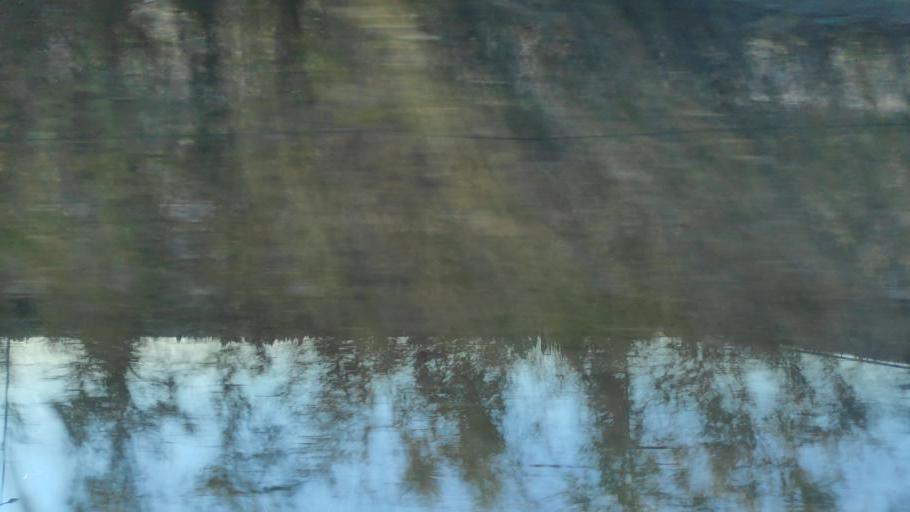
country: ES
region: Valencia
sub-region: Provincia de Castello
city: Castello de la Plana
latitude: 40.0188
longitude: -0.0137
